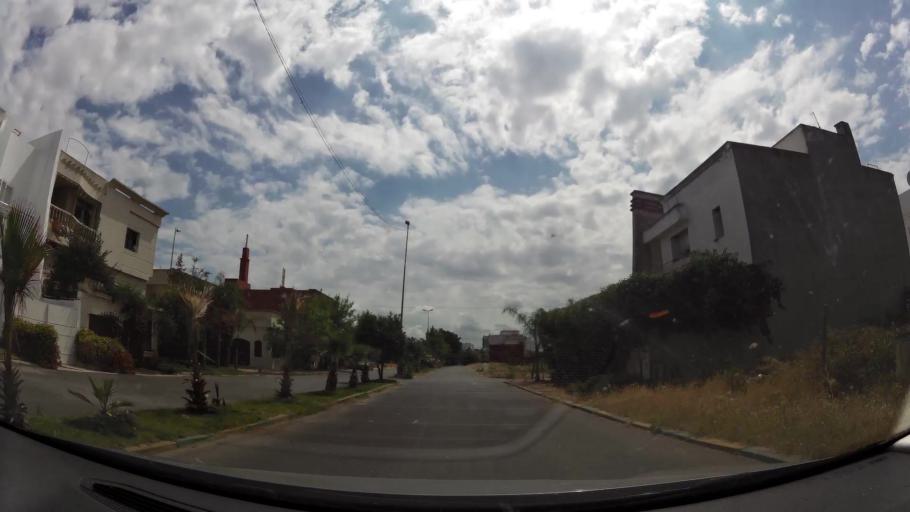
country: MA
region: Gharb-Chrarda-Beni Hssen
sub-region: Kenitra Province
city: Kenitra
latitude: 34.2430
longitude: -6.6017
